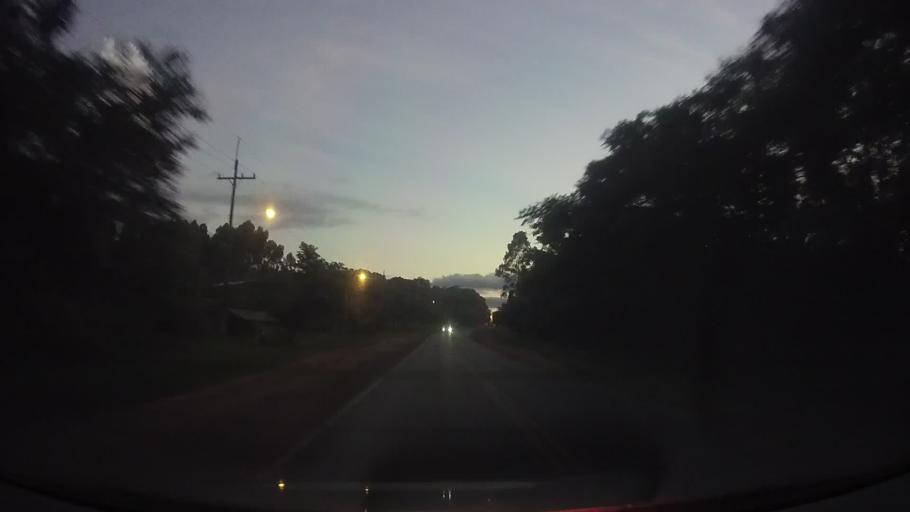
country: PY
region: Central
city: Itaugua
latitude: -25.4011
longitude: -57.3581
